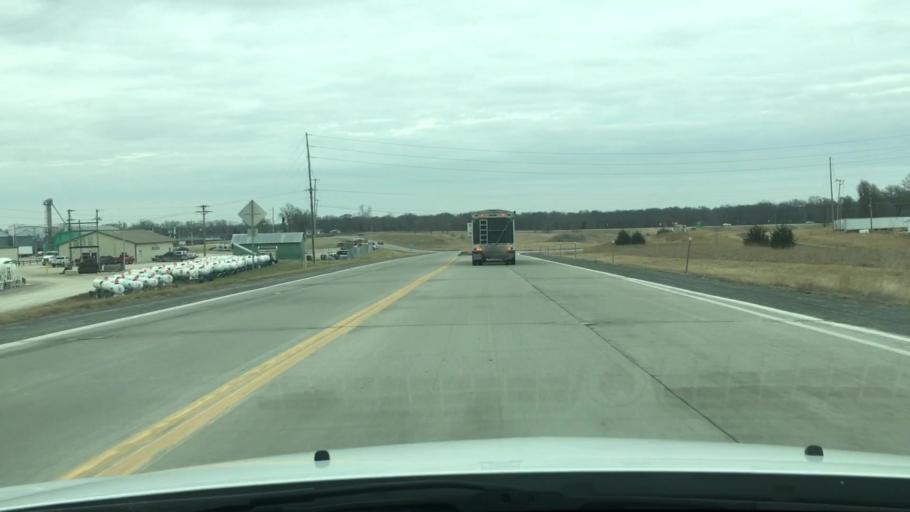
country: US
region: Missouri
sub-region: Audrain County
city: Mexico
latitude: 39.1584
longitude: -91.8428
